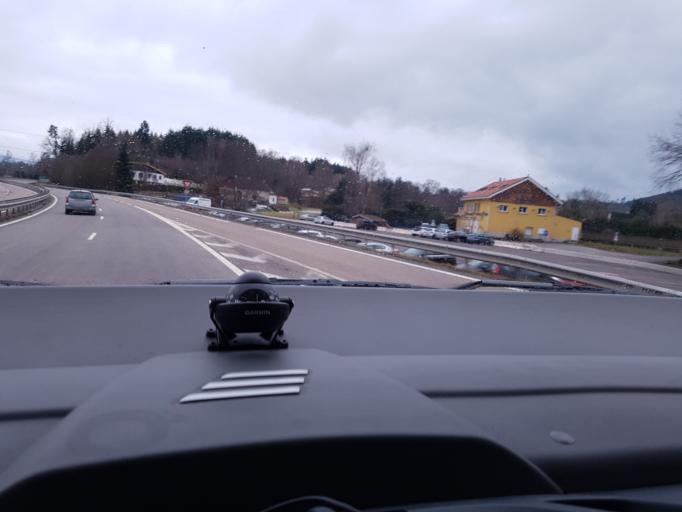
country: FR
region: Lorraine
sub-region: Departement des Vosges
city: Saulcy-sur-Meurthe
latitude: 48.2553
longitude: 6.9591
